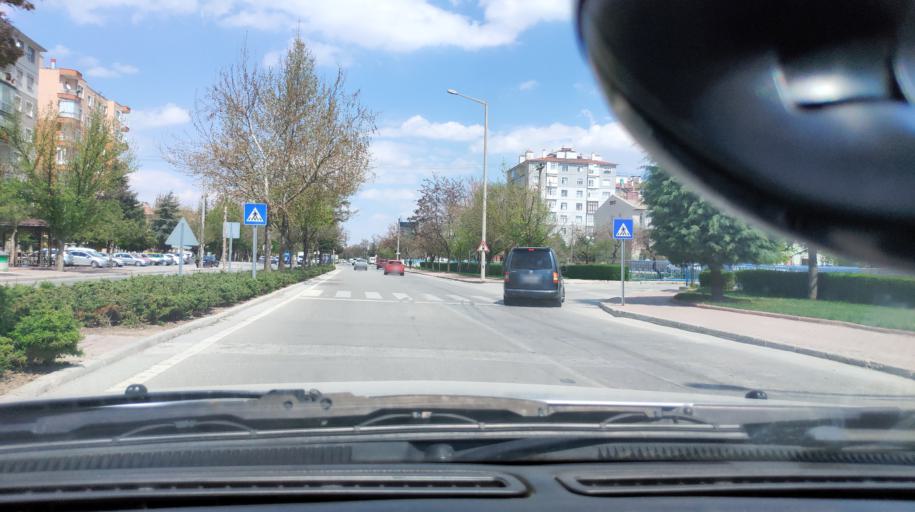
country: TR
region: Konya
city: Selcuklu
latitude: 37.9268
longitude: 32.4986
